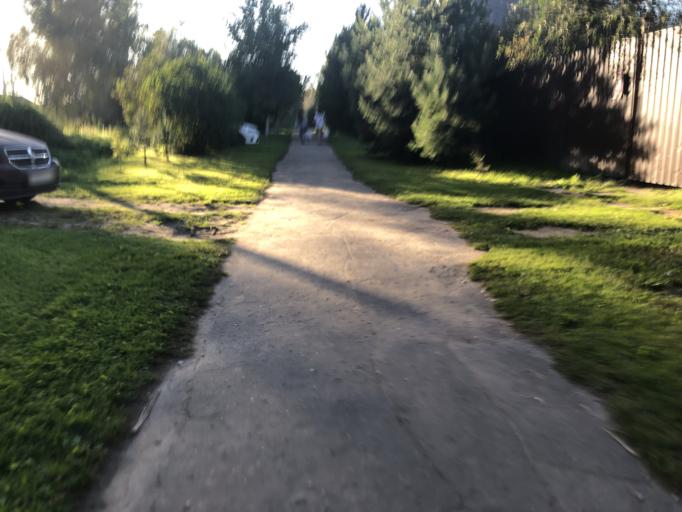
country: RU
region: Tverskaya
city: Rzhev
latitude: 56.2421
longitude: 34.3171
